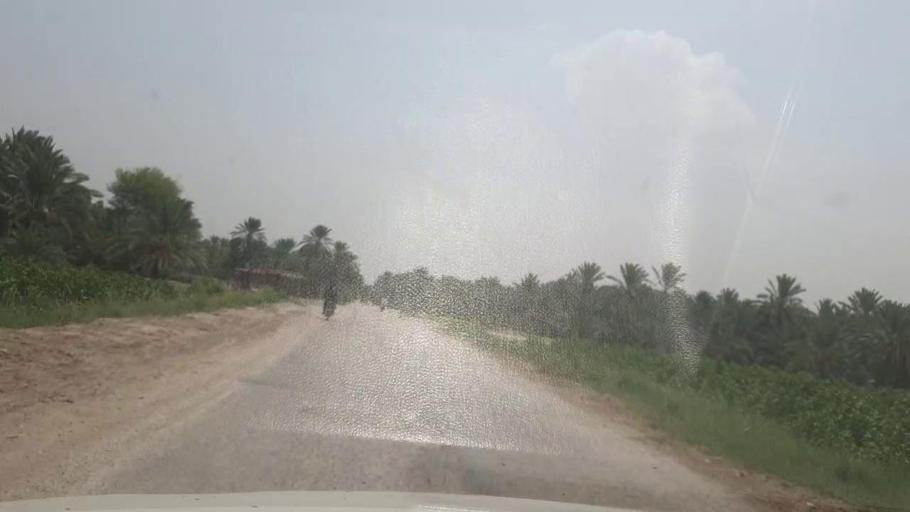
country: PK
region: Sindh
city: Kot Diji
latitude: 27.3736
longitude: 68.7153
